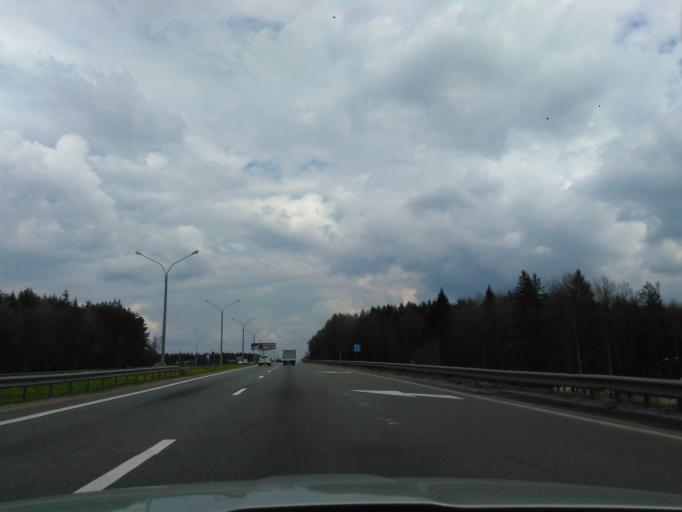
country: BY
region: Minsk
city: Kalodzishchy
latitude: 53.9647
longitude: 27.7404
